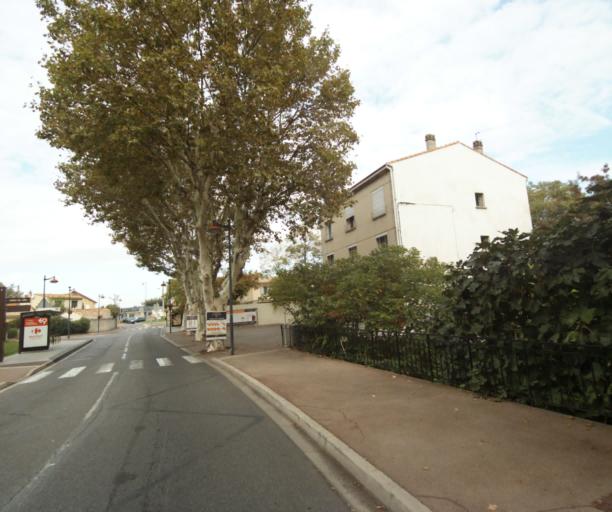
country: FR
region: Provence-Alpes-Cote d'Azur
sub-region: Departement des Bouches-du-Rhone
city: Saint-Victoret
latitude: 43.4211
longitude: 5.2331
